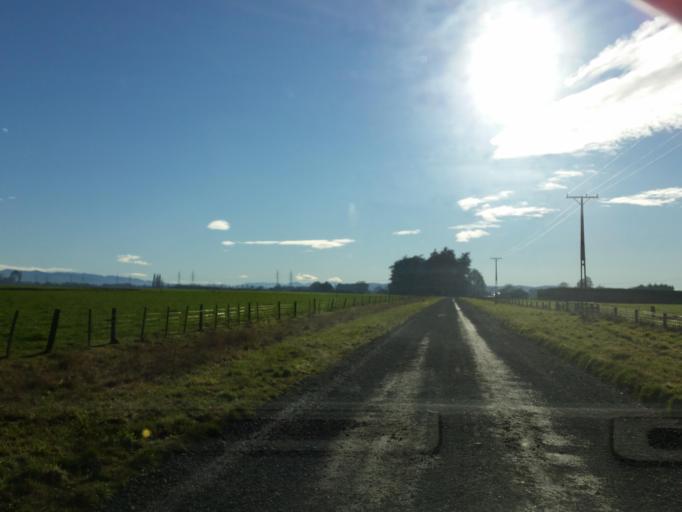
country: NZ
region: Southland
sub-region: Southland District
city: Winton
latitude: -46.1366
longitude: 168.1043
